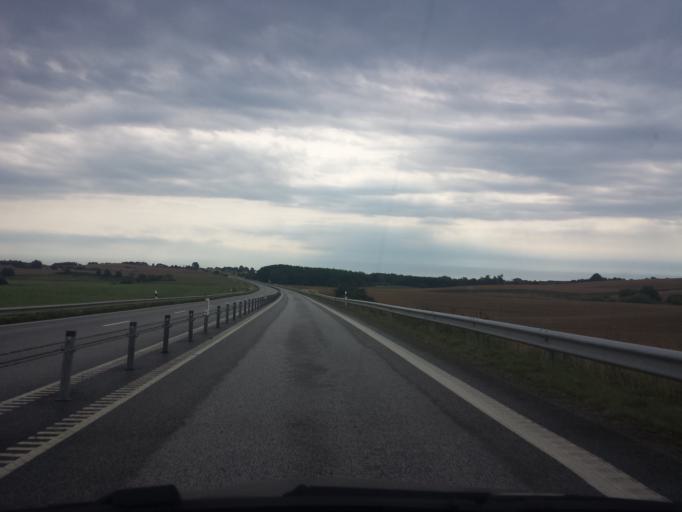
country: SE
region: Skane
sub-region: Ystads Kommun
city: Ystad
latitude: 55.4630
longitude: 13.7211
